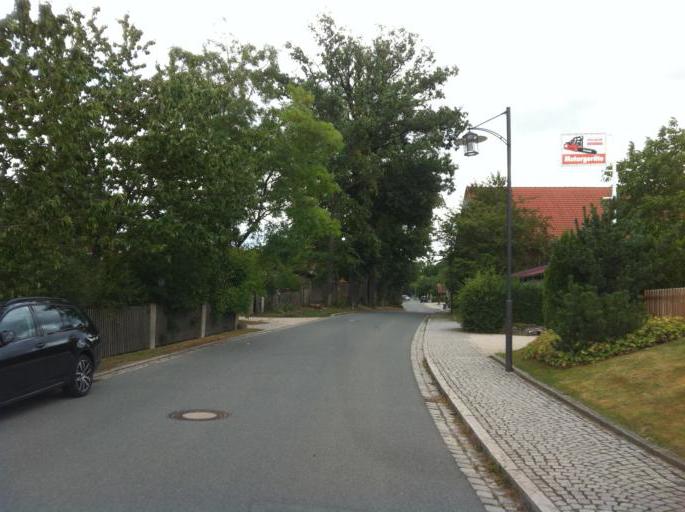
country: DE
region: Bavaria
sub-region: Upper Franconia
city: Harsdorf
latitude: 50.0180
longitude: 11.5369
